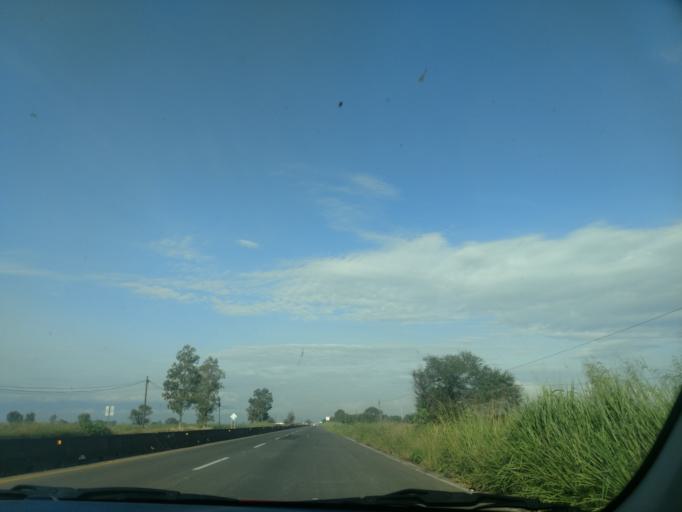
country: MX
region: Jalisco
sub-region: Ameca
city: Los Pocitos
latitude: 20.5361
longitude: -103.9474
